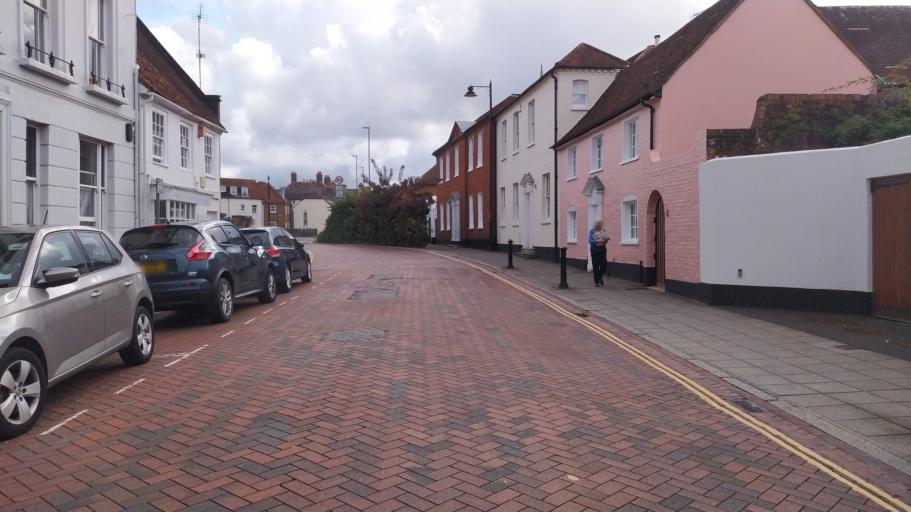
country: GB
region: England
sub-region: West Sussex
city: Chichester
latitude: 50.8369
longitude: -0.7854
